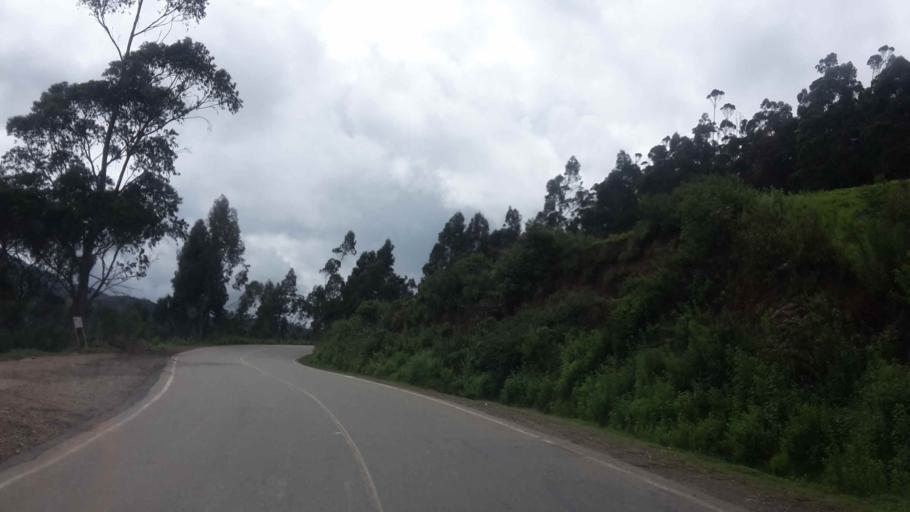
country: BO
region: Cochabamba
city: Totora
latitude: -17.5574
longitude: -65.3433
